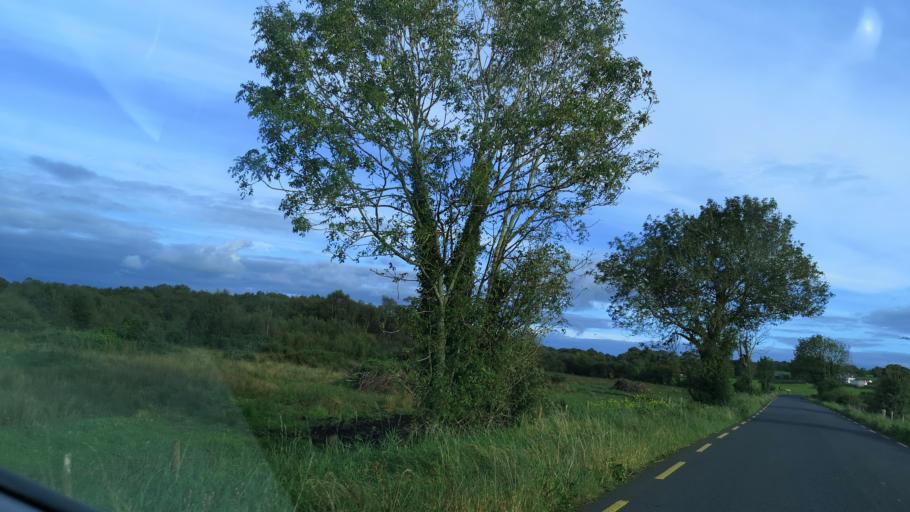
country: IE
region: Connaught
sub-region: County Galway
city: Ballinasloe
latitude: 53.3305
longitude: -8.2790
